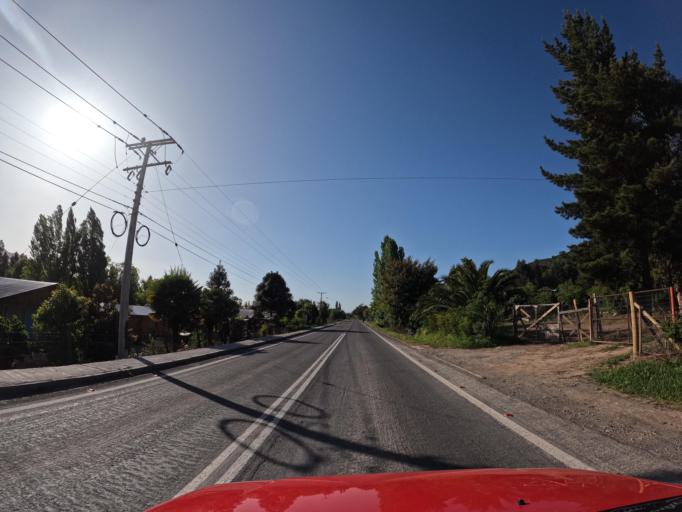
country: CL
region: Maule
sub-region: Provincia de Curico
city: Teno
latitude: -34.7973
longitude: -71.2252
